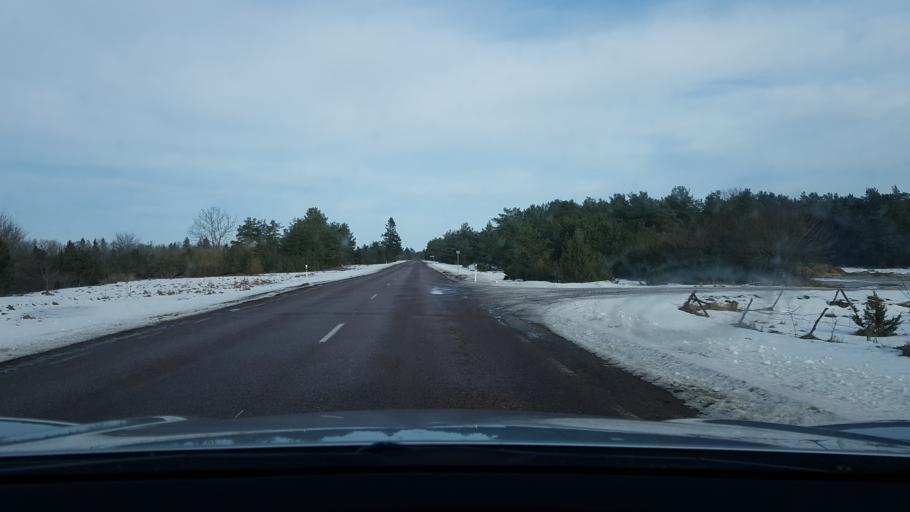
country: EE
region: Saare
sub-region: Kuressaare linn
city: Kuressaare
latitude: 58.3316
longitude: 22.5624
